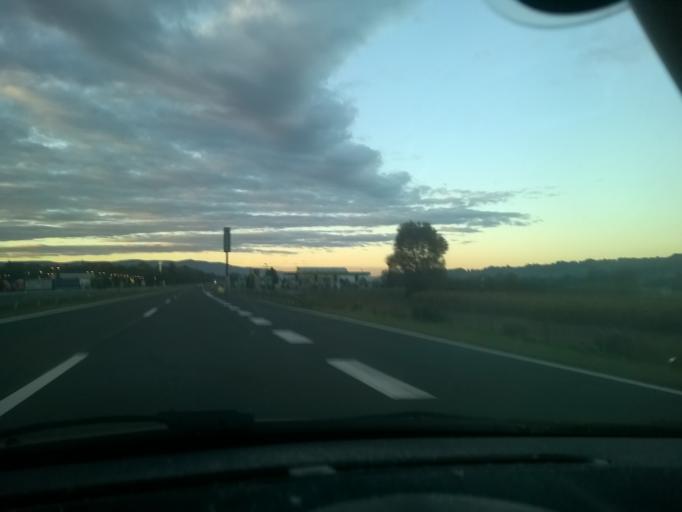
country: HR
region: Krapinsko-Zagorska
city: Zabok
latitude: 46.0692
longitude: 15.9191
